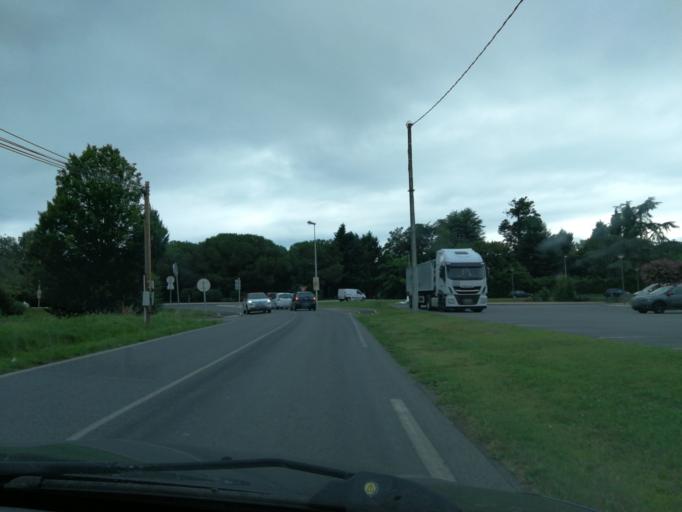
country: FR
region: Midi-Pyrenees
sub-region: Departement des Hautes-Pyrenees
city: Bazet
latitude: 43.2679
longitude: 0.0723
